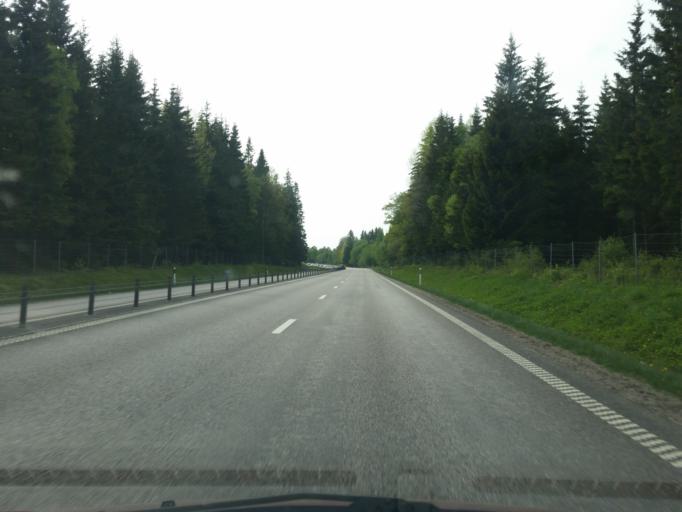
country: SE
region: Vaestra Goetaland
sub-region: Ulricehamns Kommun
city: Ulricehamn
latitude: 57.7988
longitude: 13.5288
